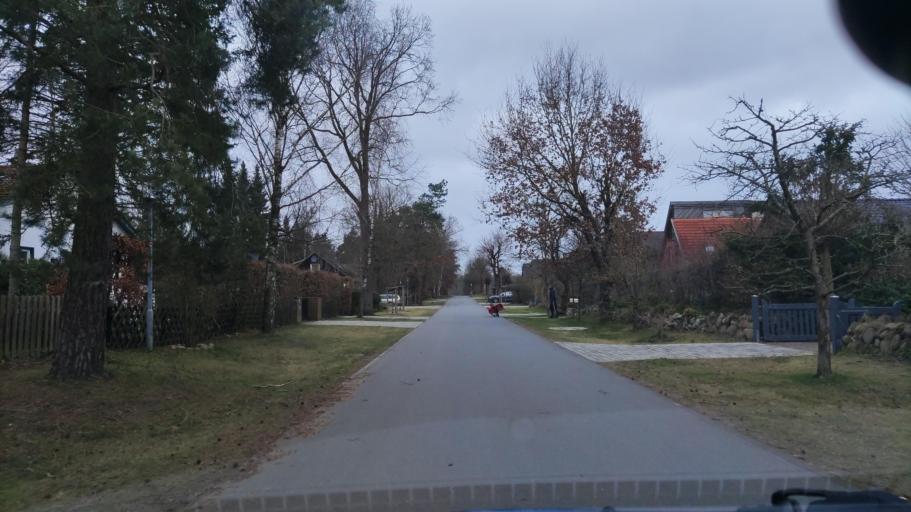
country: DE
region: Lower Saxony
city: Reppenstedt
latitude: 53.2246
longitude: 10.3347
